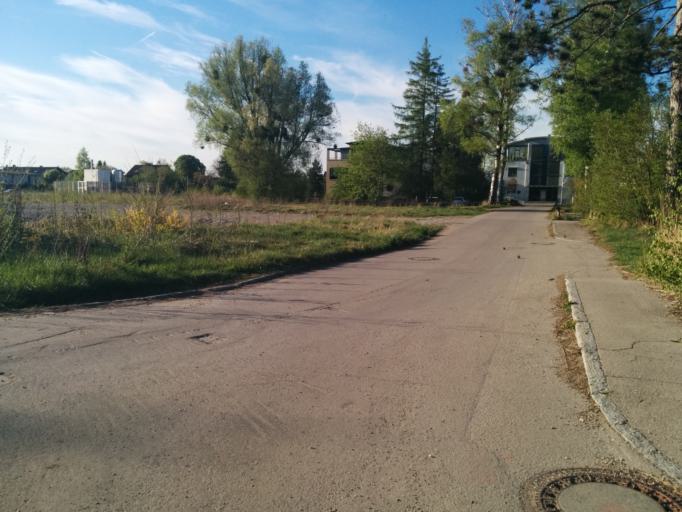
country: DE
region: Bavaria
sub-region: Upper Bavaria
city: Karlsfeld
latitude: 48.2132
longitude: 11.4576
